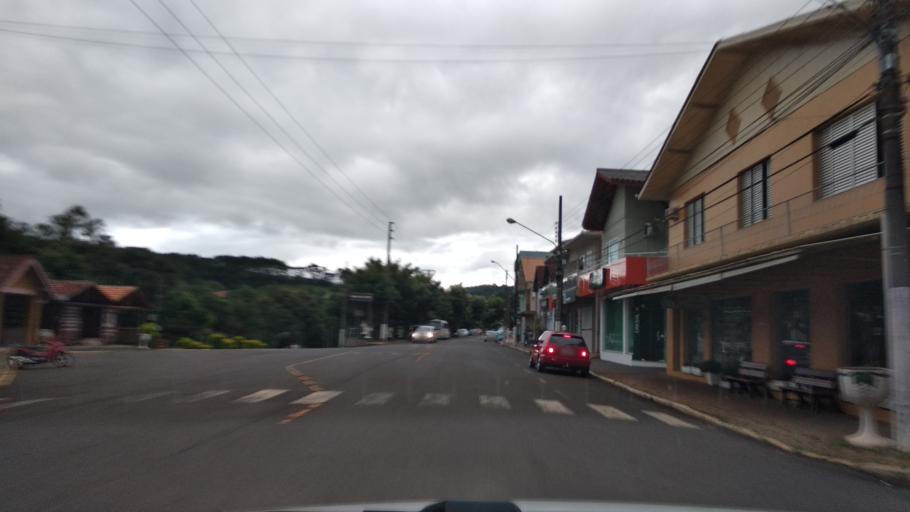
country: BR
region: Santa Catarina
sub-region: Videira
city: Videira
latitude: -27.0467
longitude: -51.2294
